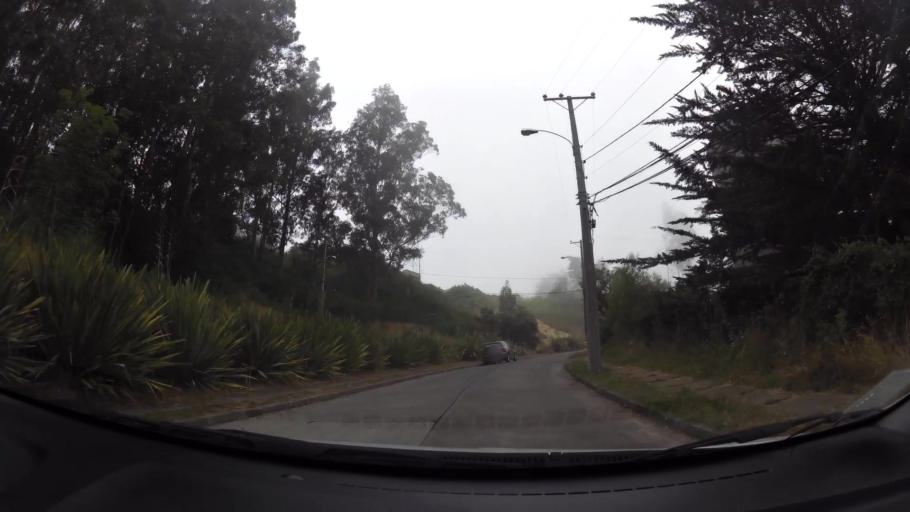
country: CL
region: Biobio
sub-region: Provincia de Concepcion
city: Concepcion
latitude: -36.8258
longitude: -73.0289
